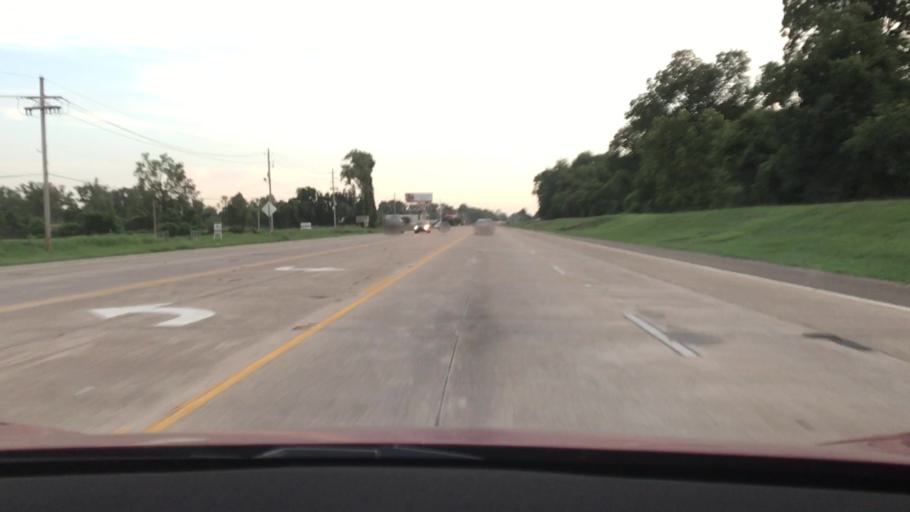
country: US
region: Louisiana
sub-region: Bossier Parish
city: Bossier City
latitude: 32.4558
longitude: -93.6916
